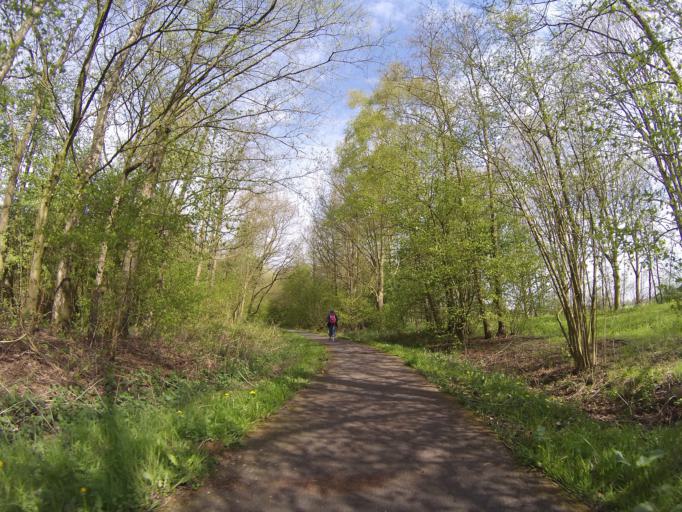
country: NL
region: Drenthe
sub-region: Gemeente Coevorden
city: Sleen
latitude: 52.8089
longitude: 6.6947
